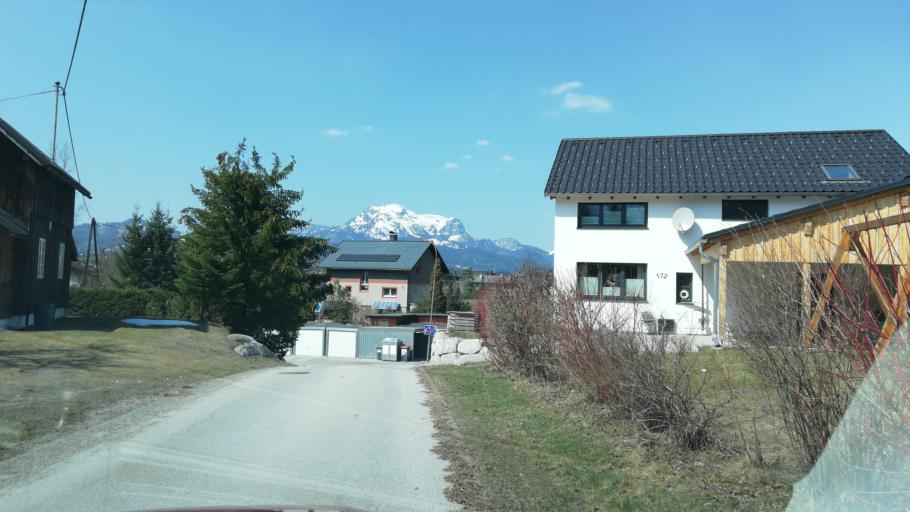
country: AT
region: Styria
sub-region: Politischer Bezirk Liezen
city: Bad Aussee
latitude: 47.5988
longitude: 13.7923
